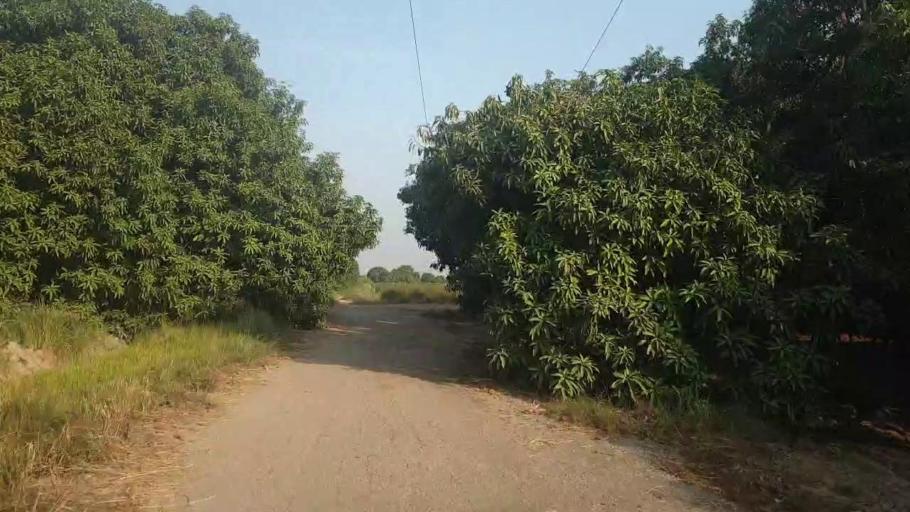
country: PK
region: Sindh
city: Tando Jam
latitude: 25.4238
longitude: 68.4686
